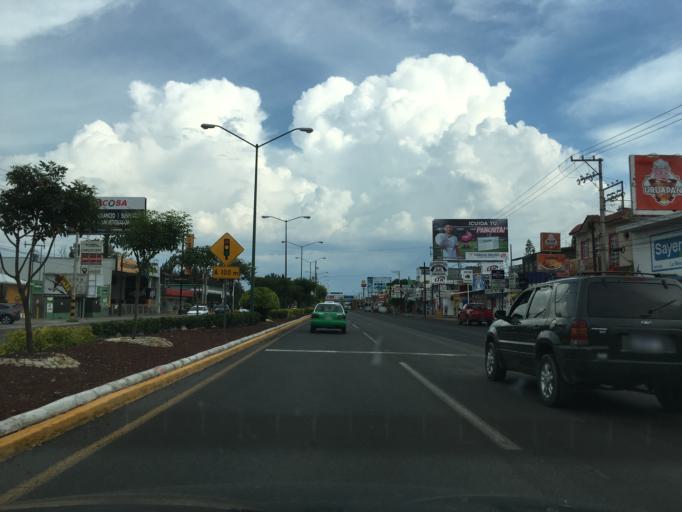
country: MX
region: Guanajuato
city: Celaya
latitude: 20.5410
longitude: -100.8205
